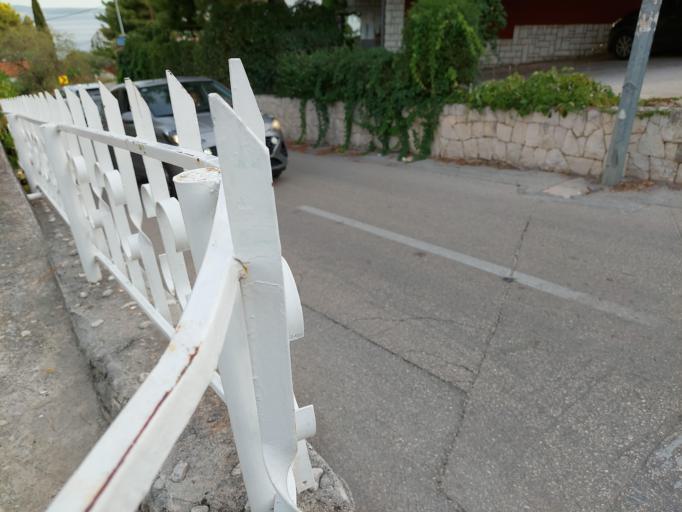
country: HR
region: Splitsko-Dalmatinska
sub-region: Grad Trogir
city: Trogir
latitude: 43.4936
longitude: 16.2707
